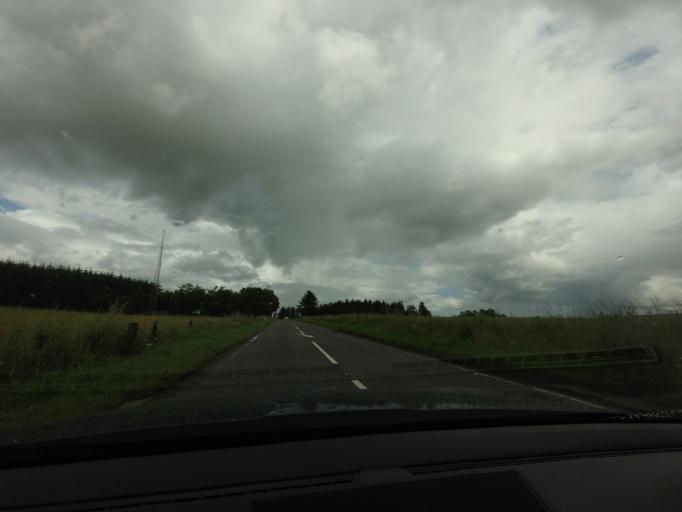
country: GB
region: Scotland
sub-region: Aberdeenshire
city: Turriff
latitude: 57.5620
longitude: -2.4369
